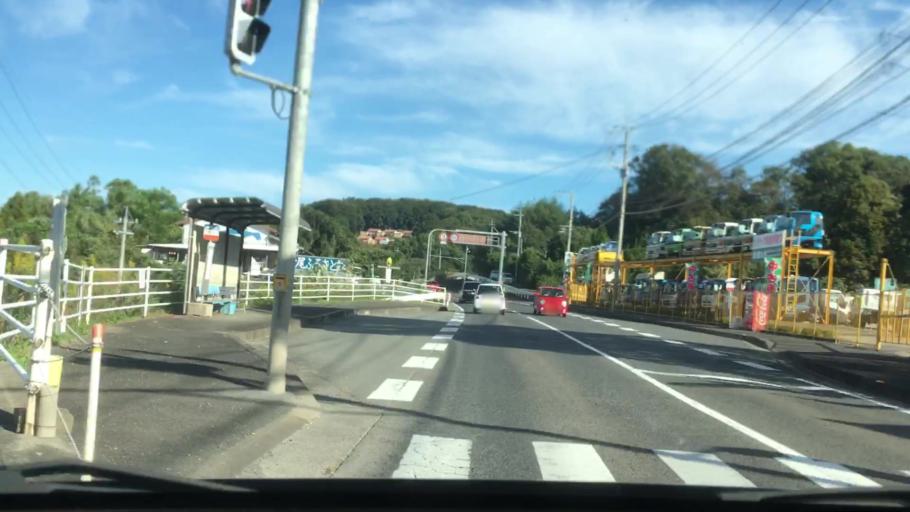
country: JP
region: Nagasaki
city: Sasebo
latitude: 33.0656
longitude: 129.7642
